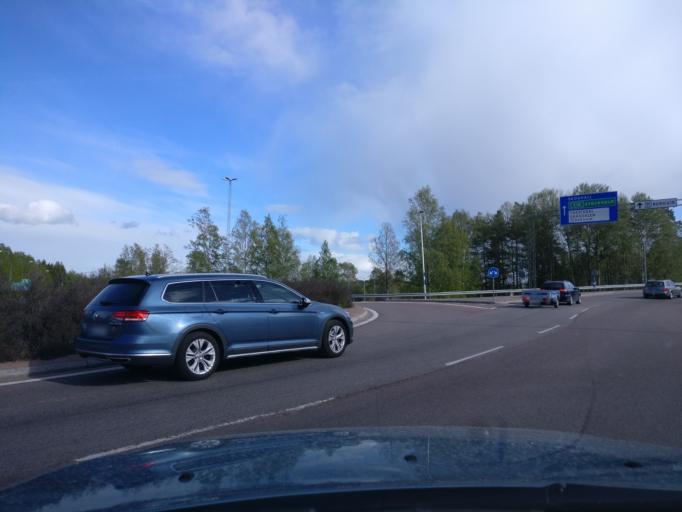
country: SE
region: Vaermland
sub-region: Hammaro Kommun
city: Skoghall
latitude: 59.3801
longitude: 13.4404
